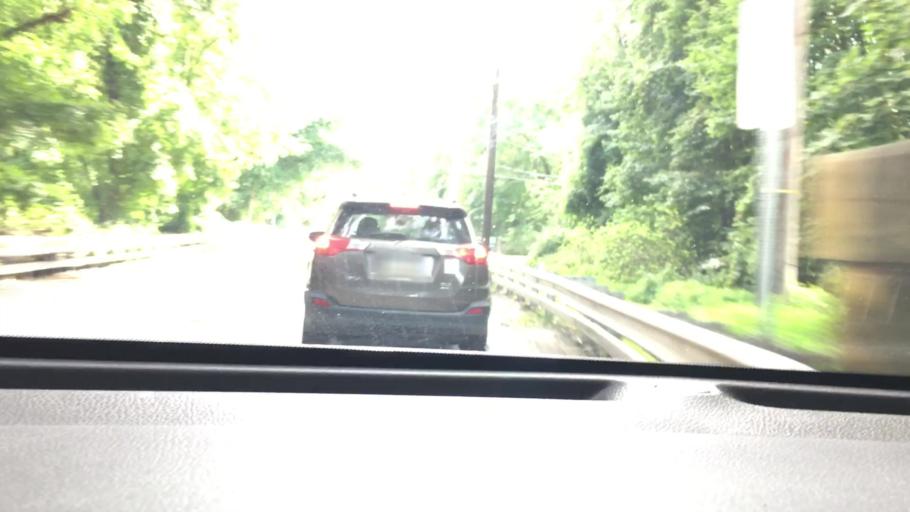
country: US
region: Pennsylvania
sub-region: Bucks County
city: Warminster Heights
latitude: 40.1604
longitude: -75.0773
